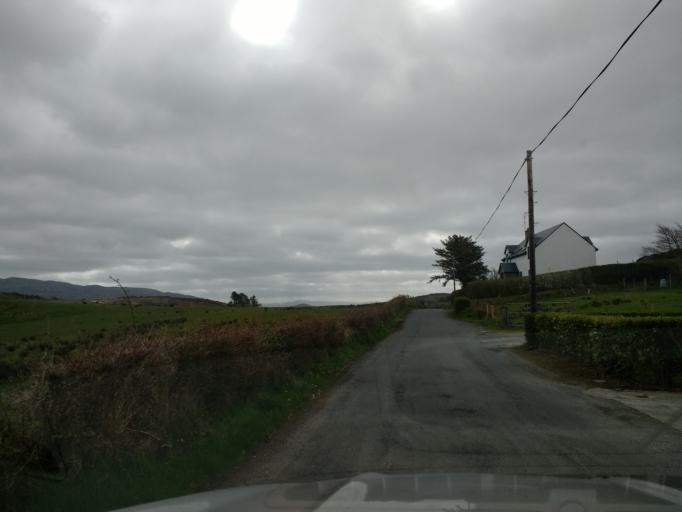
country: IE
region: Ulster
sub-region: County Donegal
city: Buncrana
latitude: 55.2440
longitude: -7.6237
